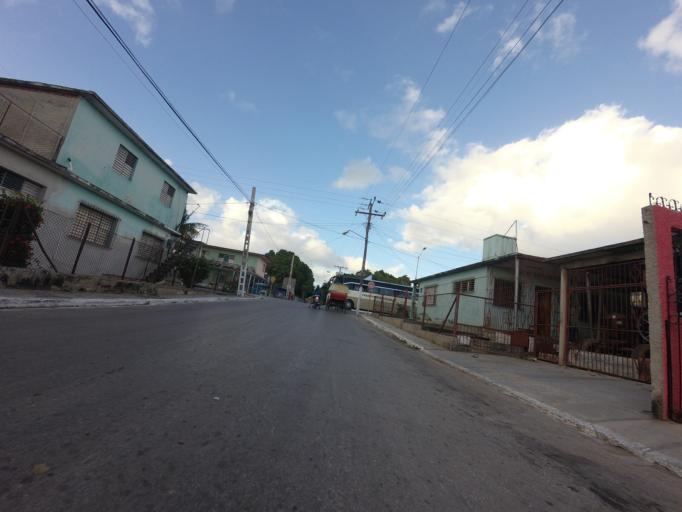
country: CU
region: Ciego de Avila
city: Ciego de Avila
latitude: 21.8381
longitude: -78.7554
